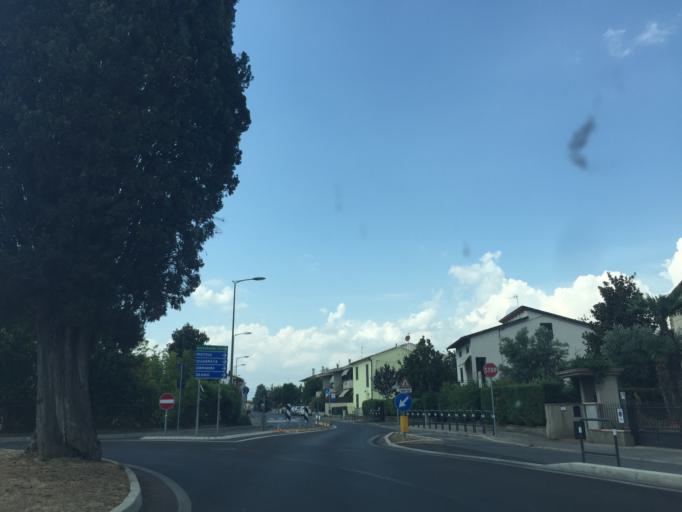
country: IT
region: Tuscany
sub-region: Provincia di Prato
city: Poggetto
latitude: 43.8252
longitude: 11.0436
